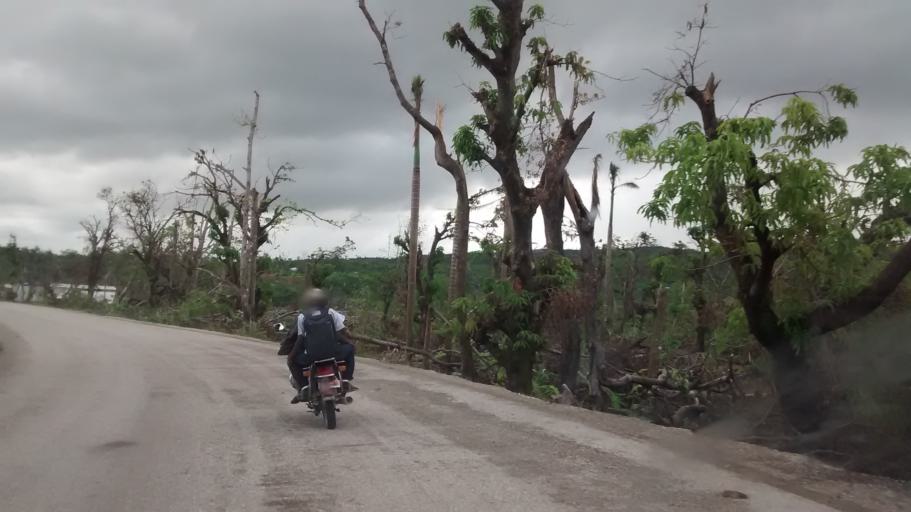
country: HT
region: Grandans
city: Jeremie
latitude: 18.6116
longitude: -74.0832
